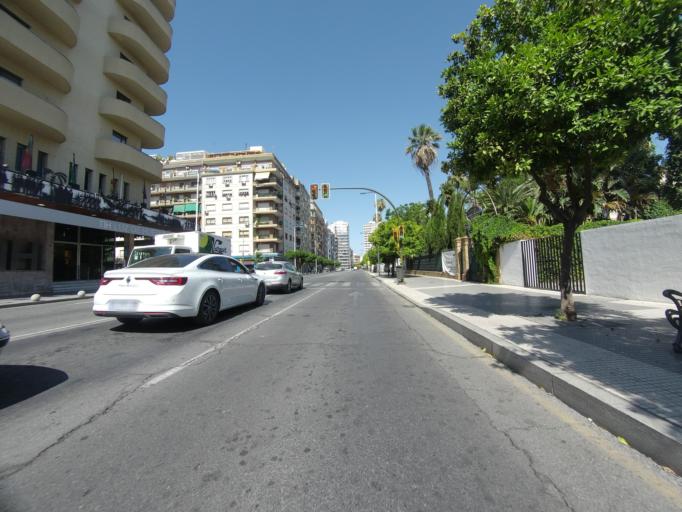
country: ES
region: Andalusia
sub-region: Provincia de Huelva
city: Huelva
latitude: 37.2546
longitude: -6.9436
